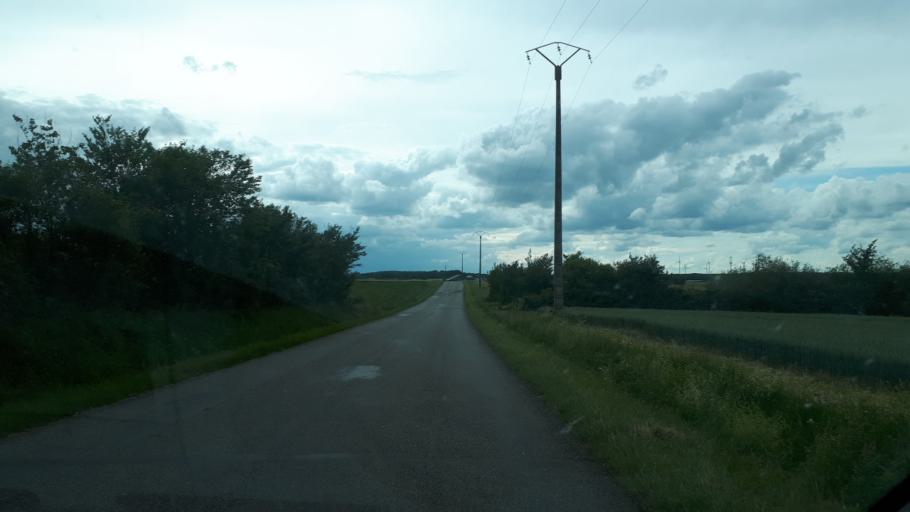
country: FR
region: Centre
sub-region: Departement de l'Indre
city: Reuilly
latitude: 47.0936
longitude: 2.0084
